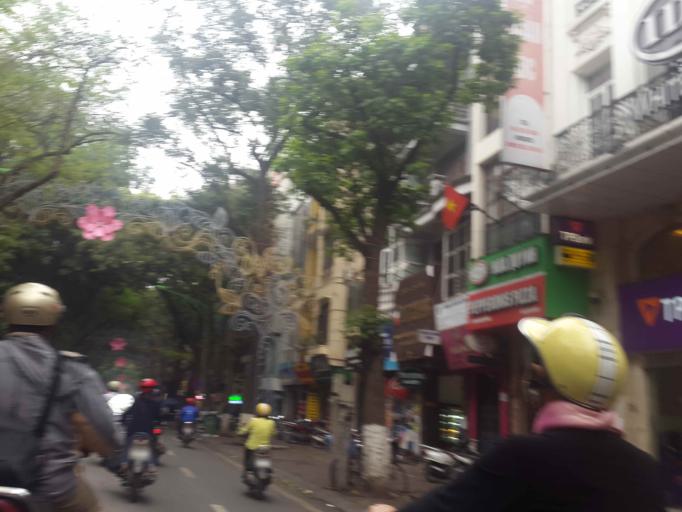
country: VN
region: Ha Noi
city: Hoan Kiem
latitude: 21.0403
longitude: 105.8434
